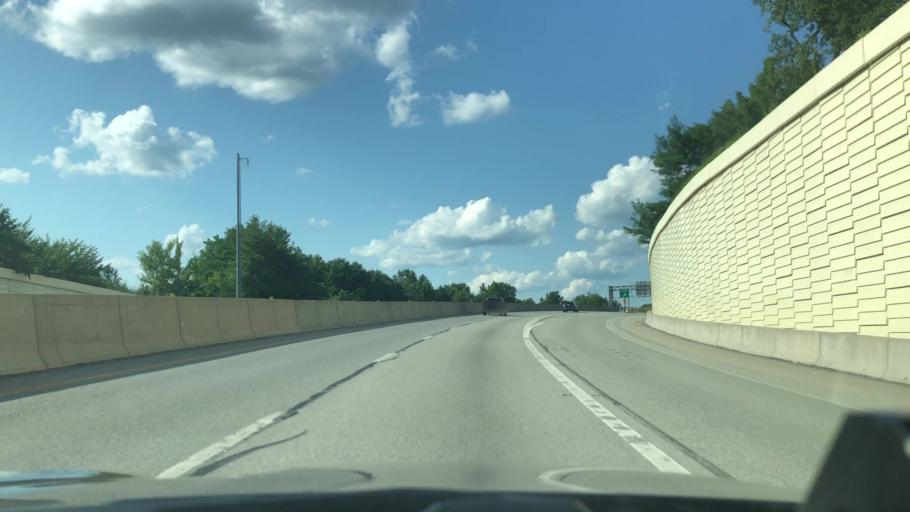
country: US
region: Pennsylvania
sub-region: Montgomery County
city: Fort Washington
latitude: 40.1454
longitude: -75.2045
